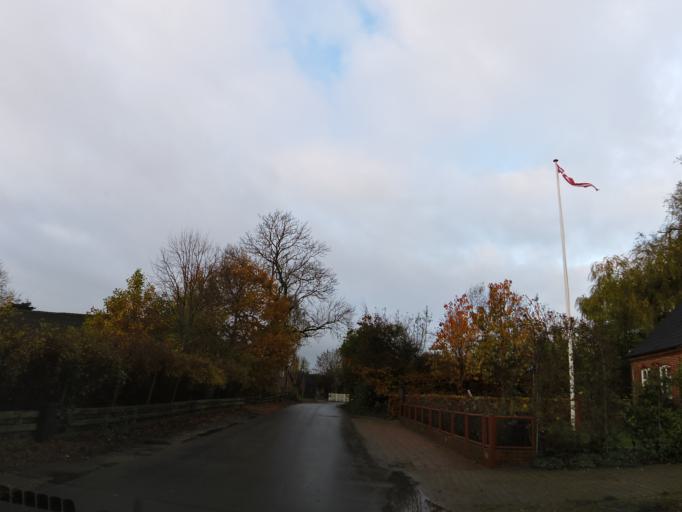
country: DK
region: Central Jutland
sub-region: Odder Kommune
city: Odder
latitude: 55.9548
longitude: 10.2417
